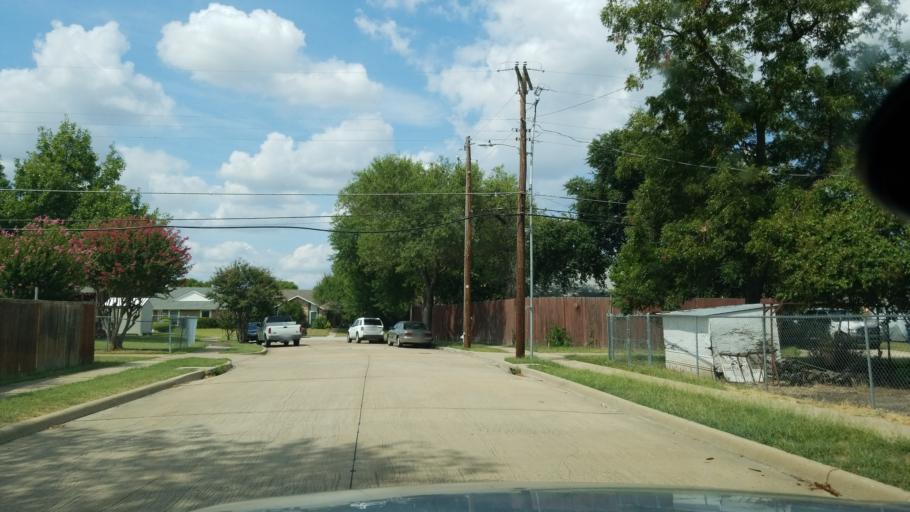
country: US
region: Texas
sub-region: Dallas County
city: Garland
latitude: 32.9195
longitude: -96.6683
